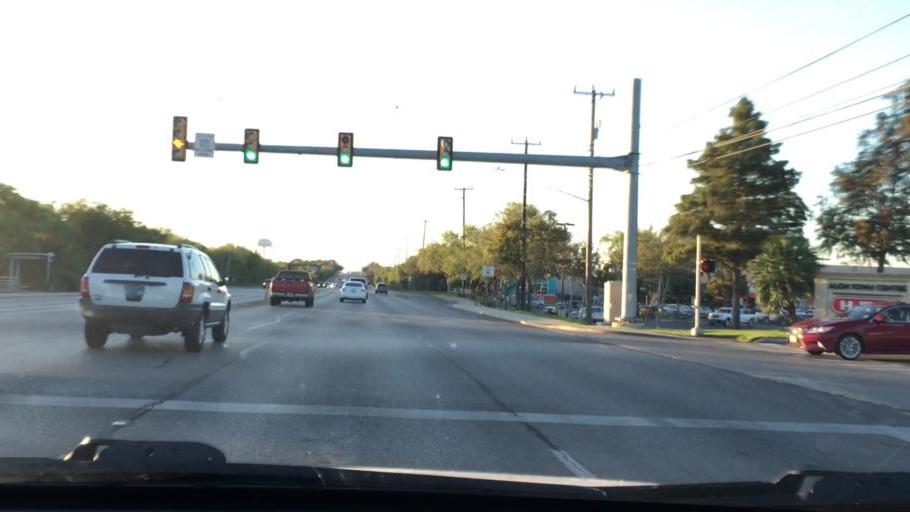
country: US
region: Texas
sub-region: Bexar County
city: Shavano Park
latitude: 29.5549
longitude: -98.5340
